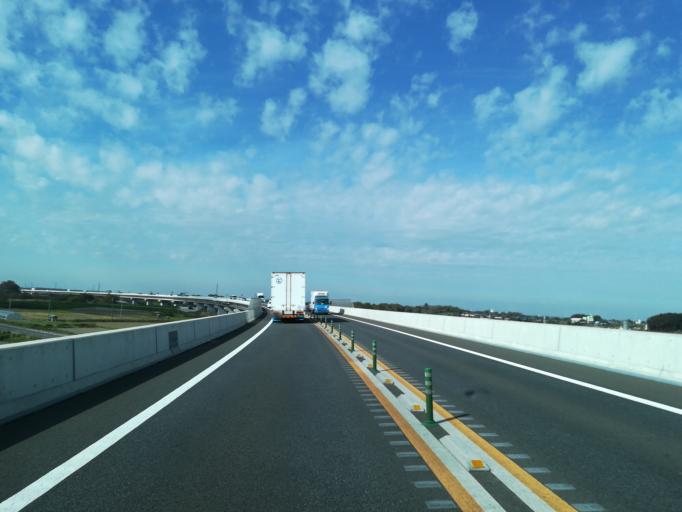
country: JP
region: Ibaraki
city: Ishige
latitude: 36.0785
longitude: 140.0095
